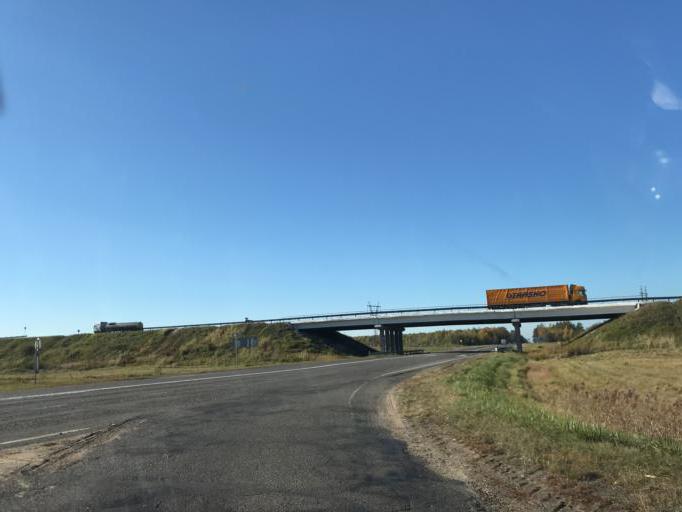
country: BY
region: Mogilev
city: Babruysk
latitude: 53.1062
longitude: 29.0582
